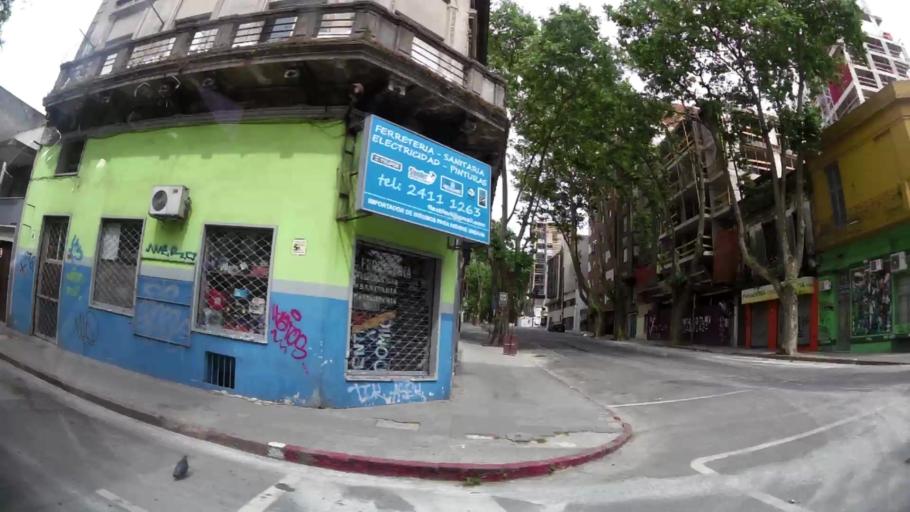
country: UY
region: Montevideo
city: Montevideo
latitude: -34.9068
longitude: -56.1785
